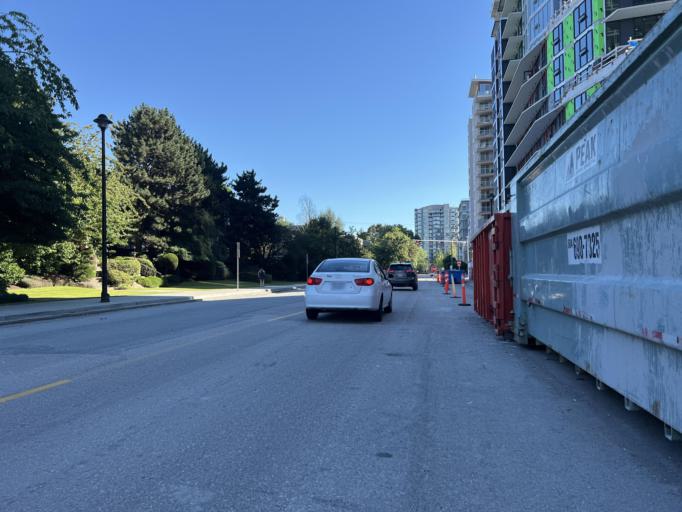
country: CA
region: British Columbia
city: Richmond
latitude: 49.1655
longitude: -123.1338
